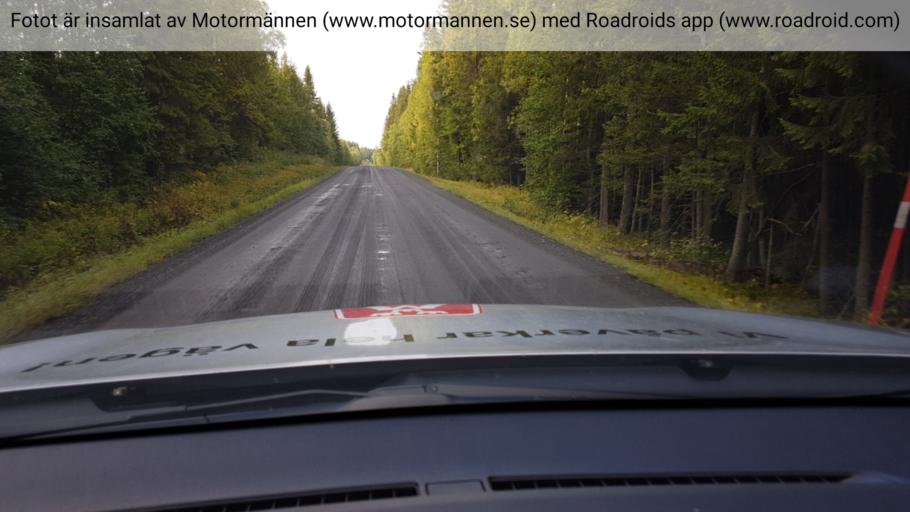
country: SE
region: Jaemtland
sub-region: Stroemsunds Kommun
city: Stroemsund
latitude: 64.1013
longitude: 15.8242
